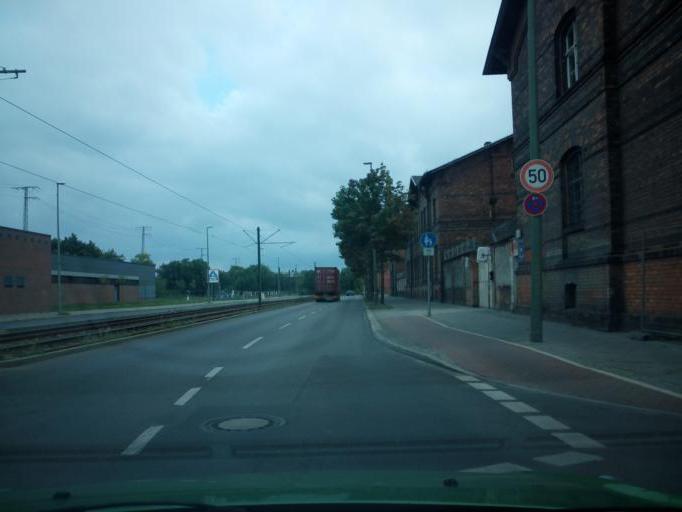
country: DE
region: Berlin
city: Rummelsburg
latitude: 52.4966
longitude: 13.4857
